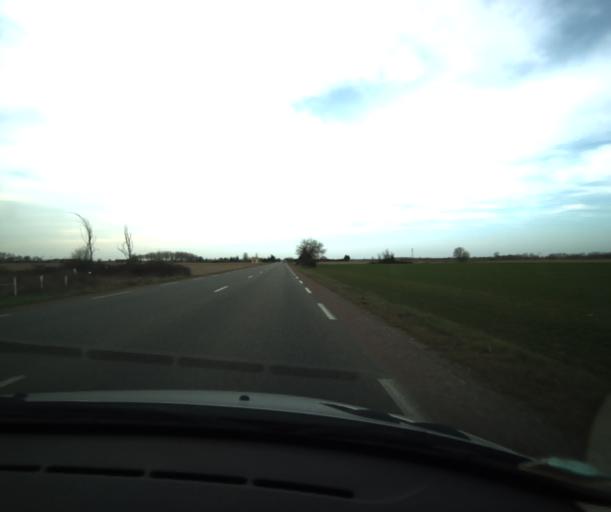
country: FR
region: Midi-Pyrenees
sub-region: Departement du Tarn-et-Garonne
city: Montech
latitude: 43.9678
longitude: 1.2070
